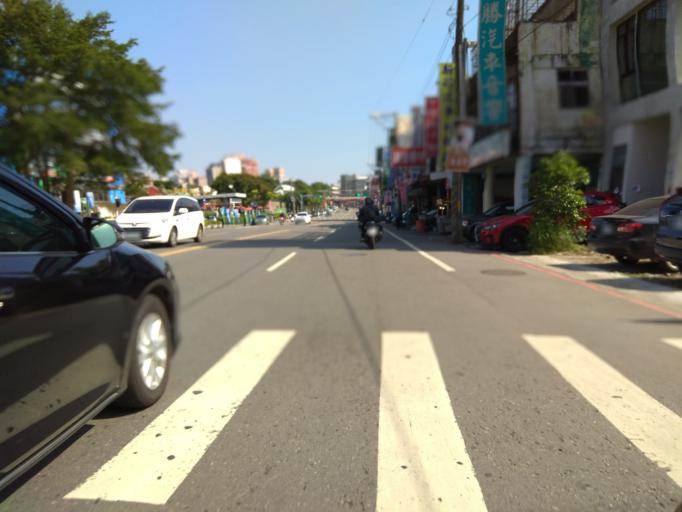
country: TW
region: Taiwan
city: Taoyuan City
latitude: 24.9504
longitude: 121.2150
